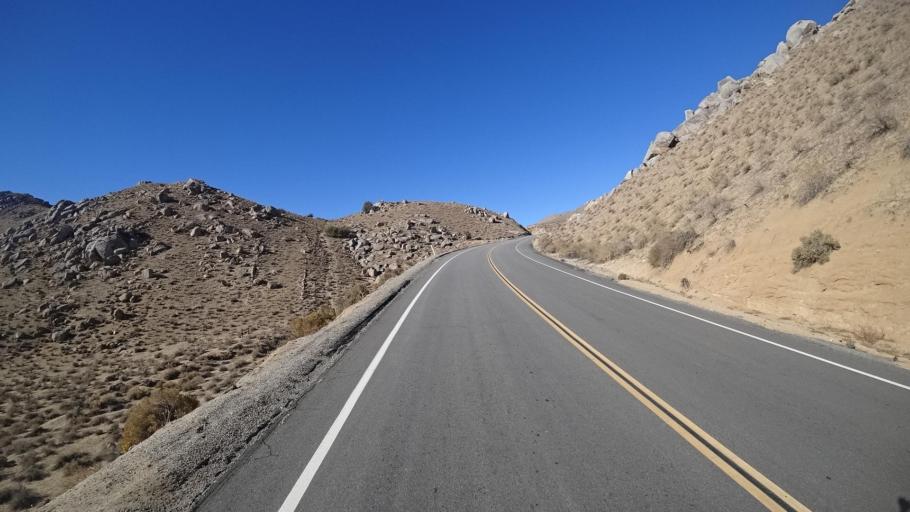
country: US
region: California
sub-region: Kern County
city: Weldon
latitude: 35.6743
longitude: -118.3559
